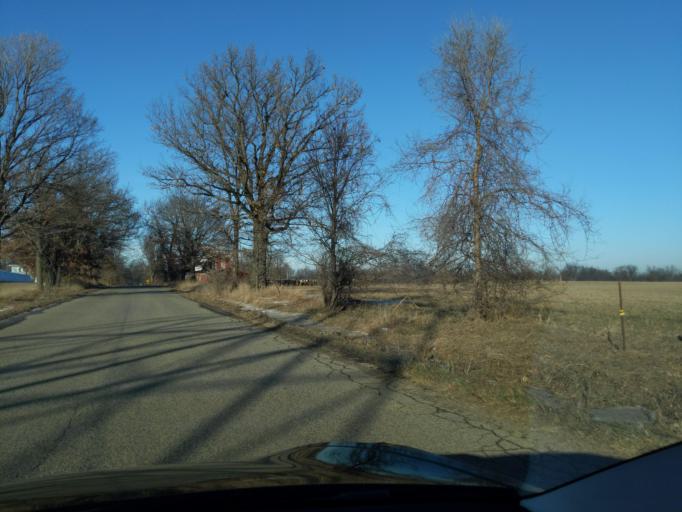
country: US
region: Michigan
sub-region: Ingham County
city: Stockbridge
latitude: 42.4207
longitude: -84.1509
